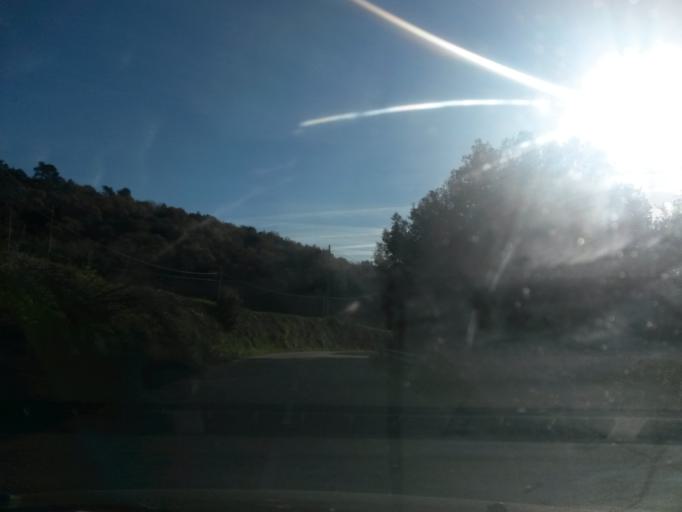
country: ES
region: Catalonia
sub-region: Provincia de Girona
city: la Cellera de Ter
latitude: 41.9690
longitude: 2.6309
